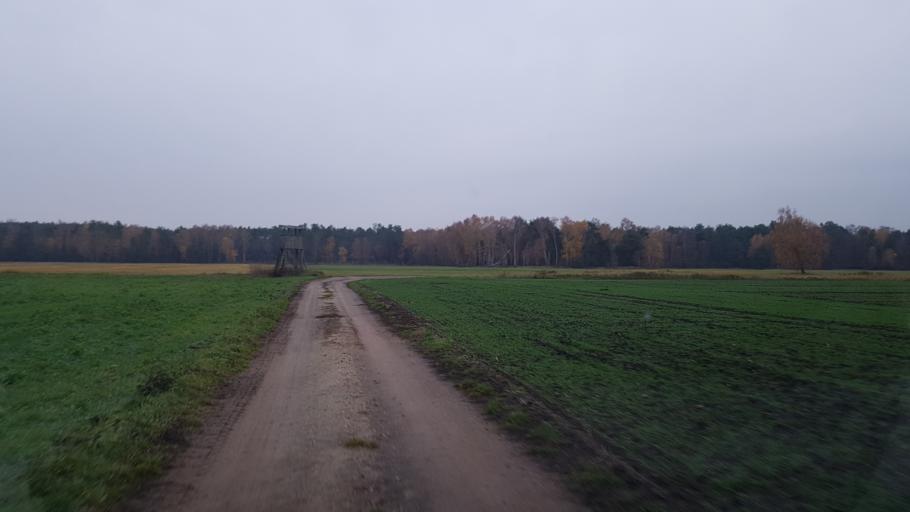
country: DE
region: Brandenburg
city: Trobitz
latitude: 51.6494
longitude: 13.4128
